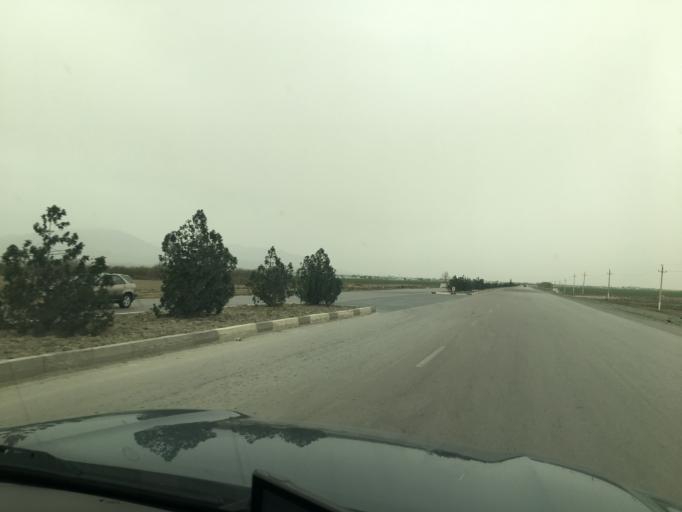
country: TM
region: Ahal
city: Baharly
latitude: 38.3843
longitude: 57.4962
